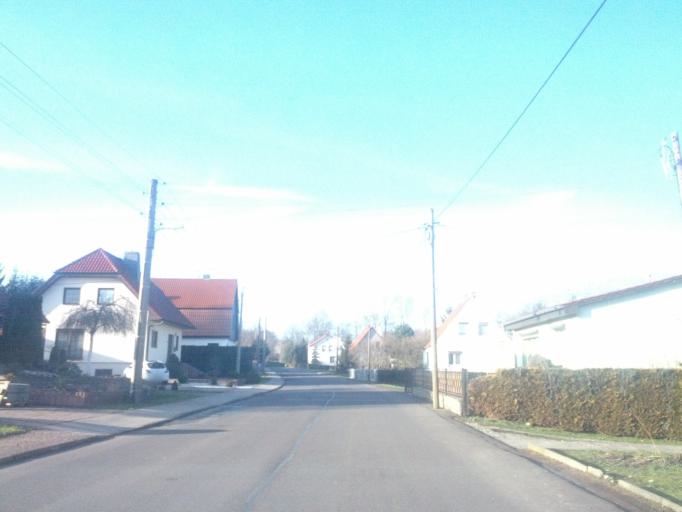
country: DE
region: Thuringia
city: Horselgau
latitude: 50.9271
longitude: 10.5767
